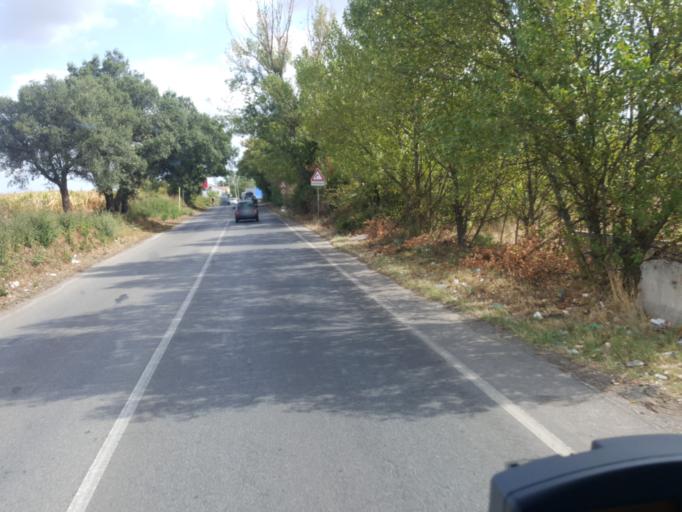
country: IT
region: Latium
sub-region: Citta metropolitana di Roma Capitale
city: Area Produttiva
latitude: 41.6936
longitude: 12.5215
